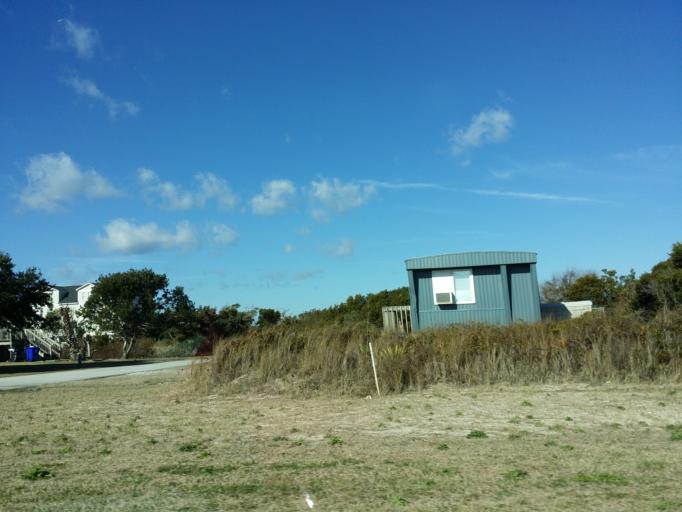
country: US
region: North Carolina
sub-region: Pender County
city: Surf City
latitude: 34.4637
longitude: -77.4810
